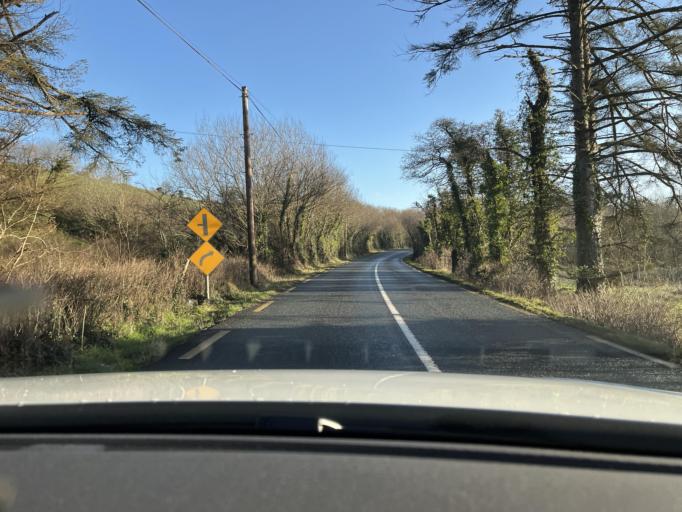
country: IE
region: Connaught
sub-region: County Leitrim
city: Manorhamilton
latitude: 54.2355
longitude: -8.2097
